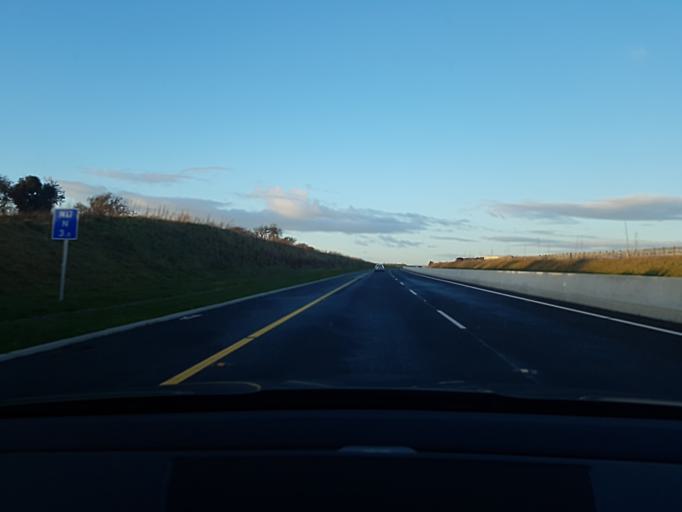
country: IE
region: Connaught
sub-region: County Galway
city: Athenry
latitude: 53.3277
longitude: -8.8032
